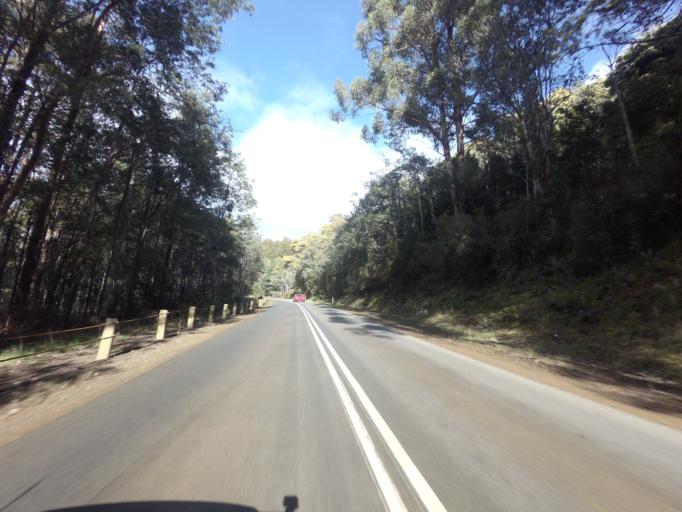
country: AU
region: Tasmania
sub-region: Huon Valley
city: Geeveston
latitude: -43.3434
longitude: 146.9628
